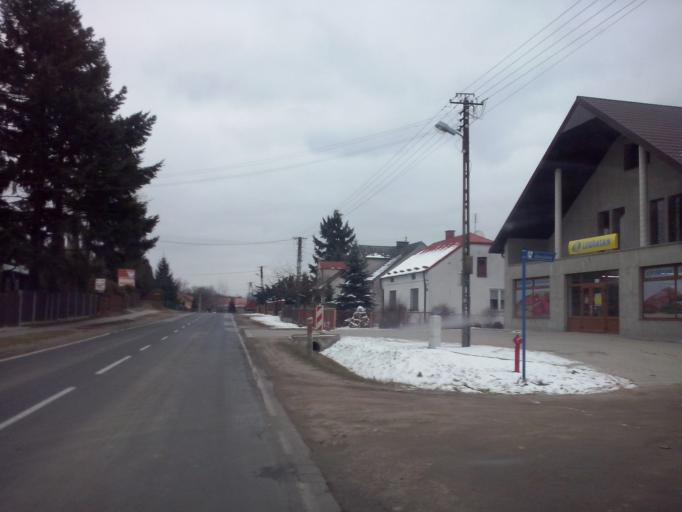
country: PL
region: Subcarpathian Voivodeship
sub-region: Powiat nizanski
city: Zarzecze
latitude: 50.5228
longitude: 22.2063
